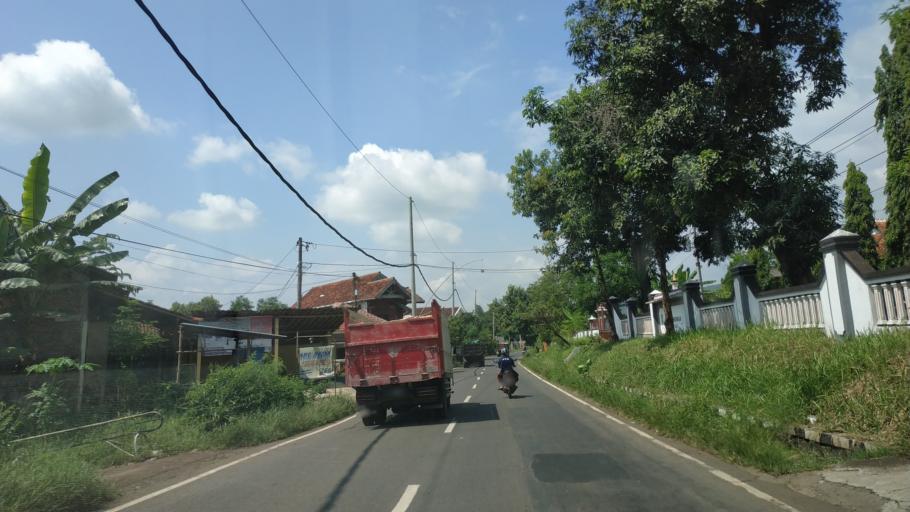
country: ID
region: Central Java
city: Weleri
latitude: -6.9869
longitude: 110.0726
